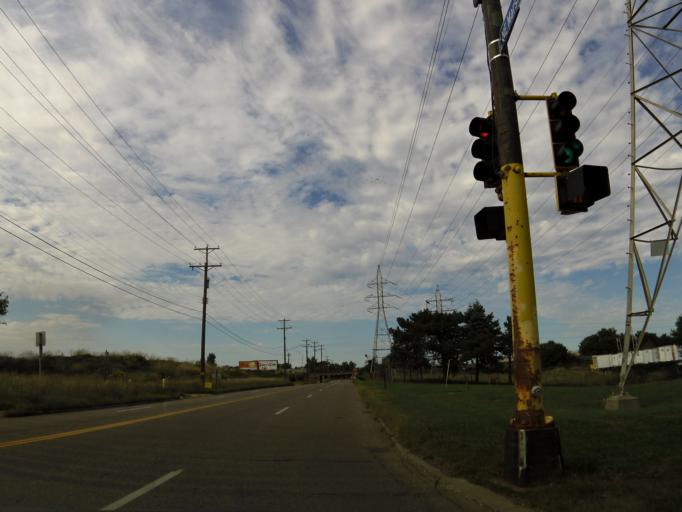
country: US
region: Minnesota
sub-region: Anoka County
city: Columbia Heights
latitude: 45.0276
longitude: -93.2757
